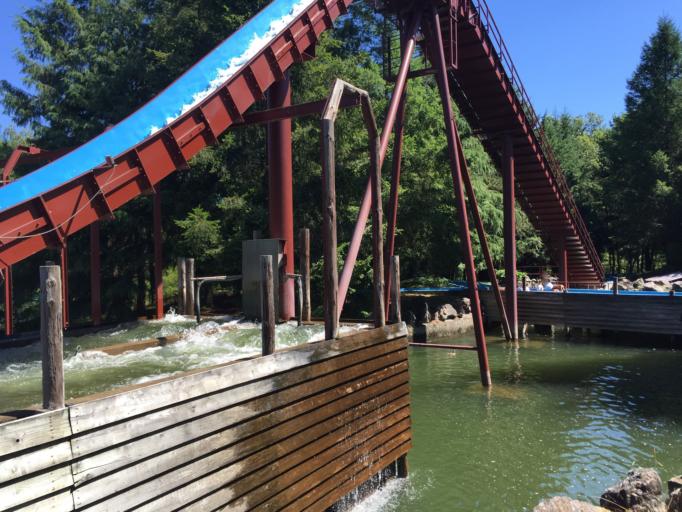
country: FR
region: Auvergne
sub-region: Departement de l'Allier
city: Dompierre-sur-Besbre
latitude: 46.5092
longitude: 3.6332
